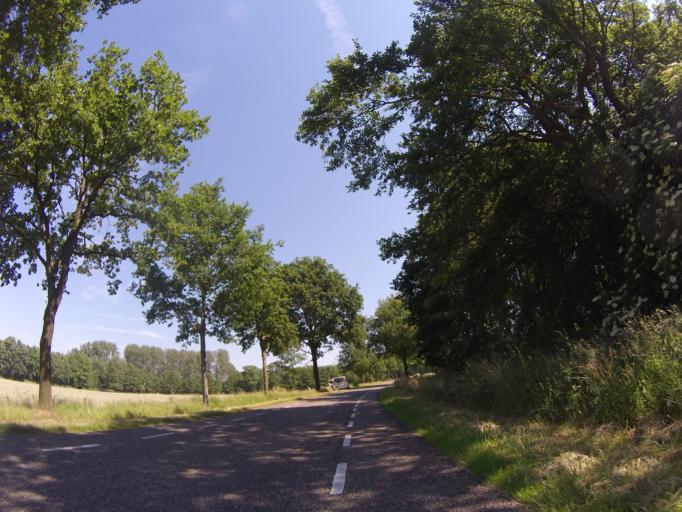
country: NL
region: Drenthe
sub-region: Gemeente Coevorden
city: Sleen
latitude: 52.8069
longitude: 6.7346
